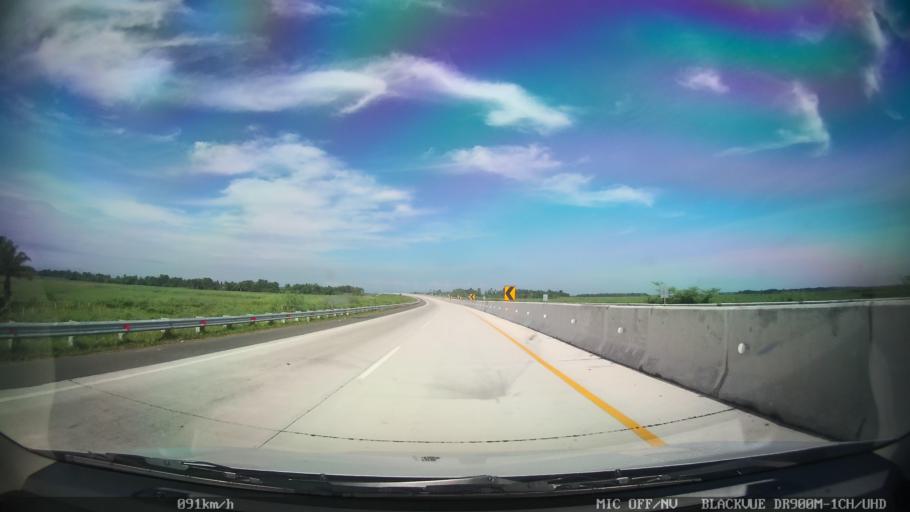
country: ID
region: North Sumatra
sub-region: Kabupaten Langkat
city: Stabat
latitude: 3.7117
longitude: 98.5299
